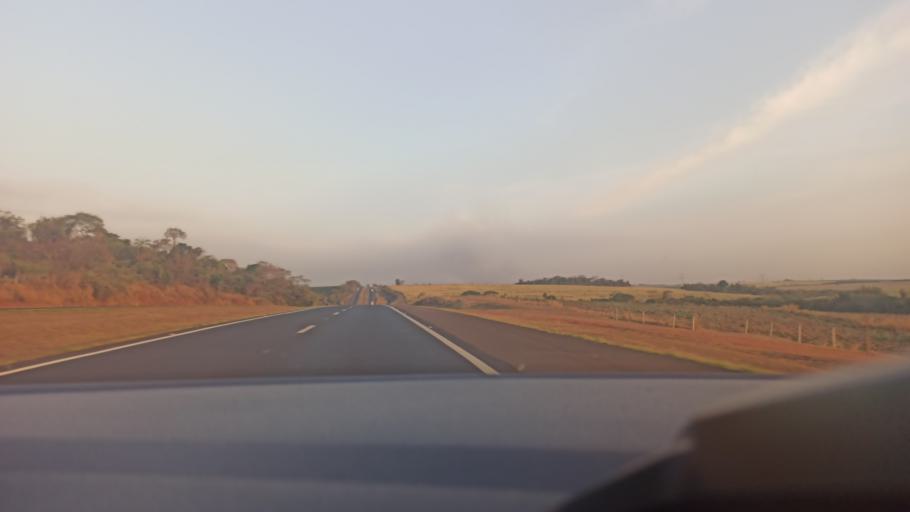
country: BR
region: Sao Paulo
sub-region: Taquaritinga
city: Taquaritinga
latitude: -21.4309
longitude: -48.6635
